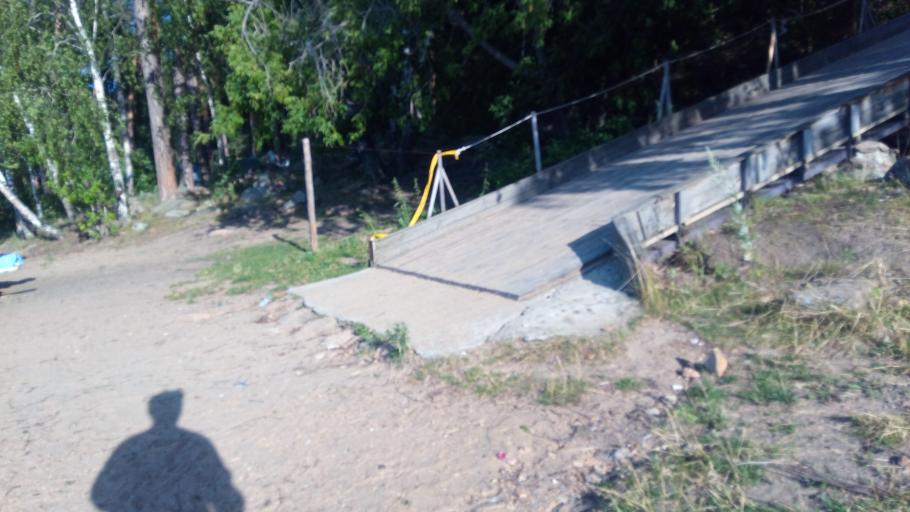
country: RU
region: Chelyabinsk
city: Chebarkul'
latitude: 55.0217
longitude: 60.3133
